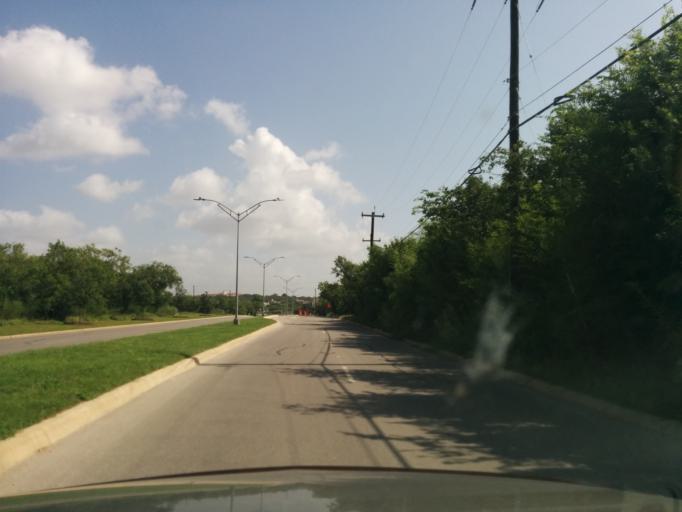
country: US
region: Texas
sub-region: Bexar County
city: Shavano Park
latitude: 29.5697
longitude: -98.6176
